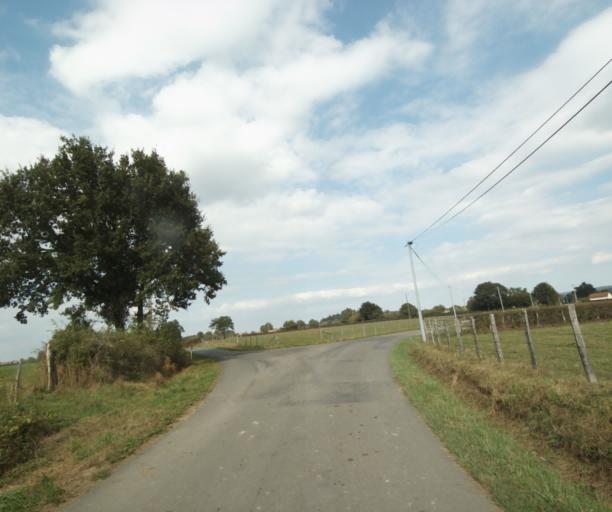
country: FR
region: Bourgogne
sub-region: Departement de Saone-et-Loire
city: Palinges
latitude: 46.4949
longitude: 4.2008
